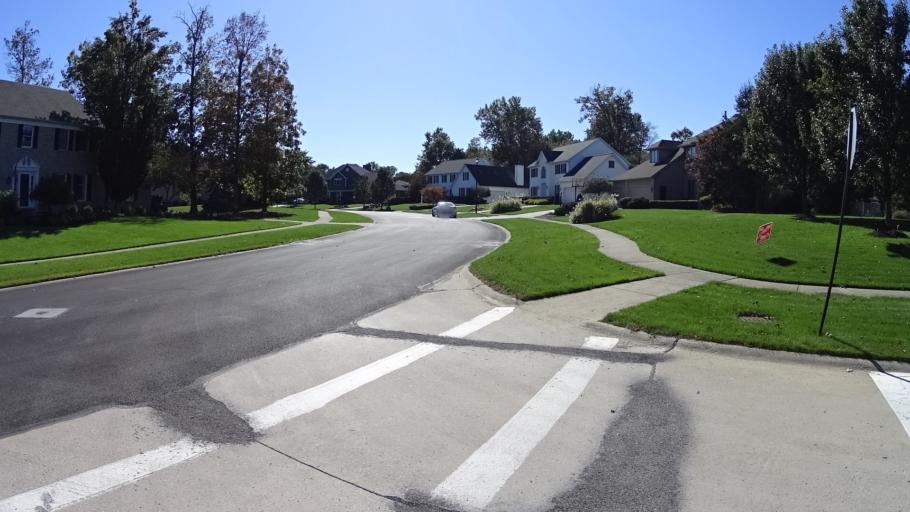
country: US
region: Ohio
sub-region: Lorain County
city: Amherst
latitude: 41.3851
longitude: -82.2275
